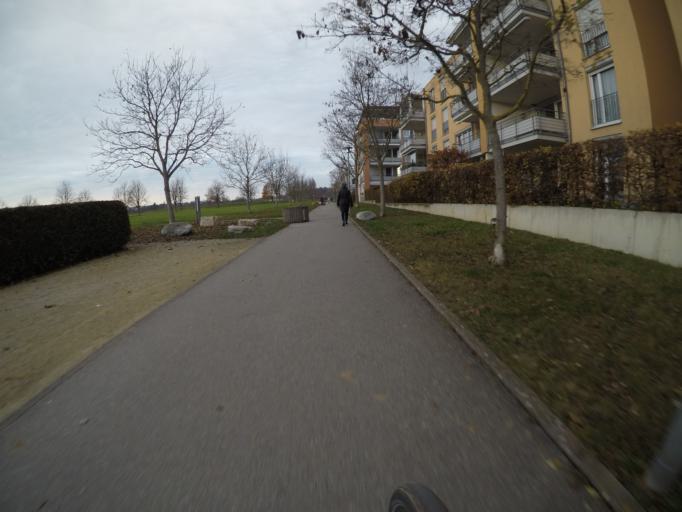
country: DE
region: Baden-Wuerttemberg
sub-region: Regierungsbezirk Stuttgart
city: Ostfildern
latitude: 48.7186
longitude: 9.2666
